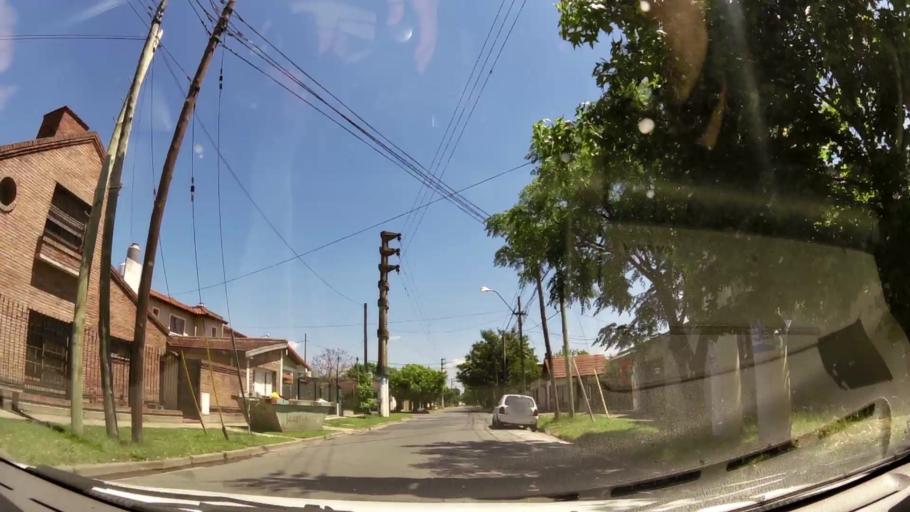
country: AR
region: Buenos Aires
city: Ituzaingo
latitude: -34.6581
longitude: -58.6781
